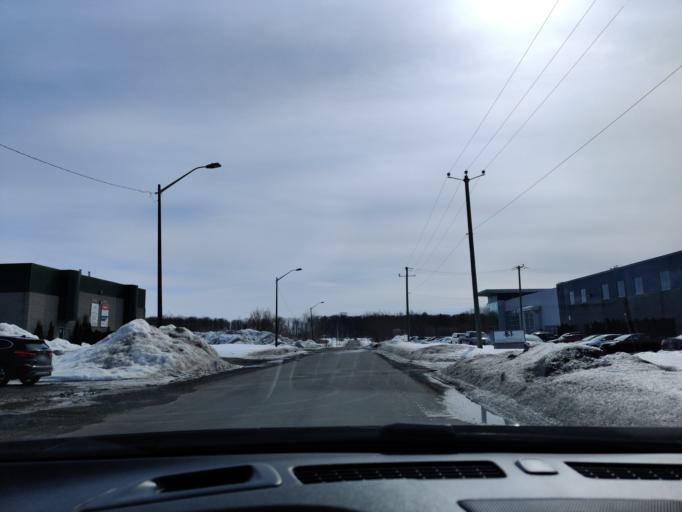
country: CA
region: Quebec
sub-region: Laurentides
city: Saint-Jerome
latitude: 45.7565
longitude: -73.9924
